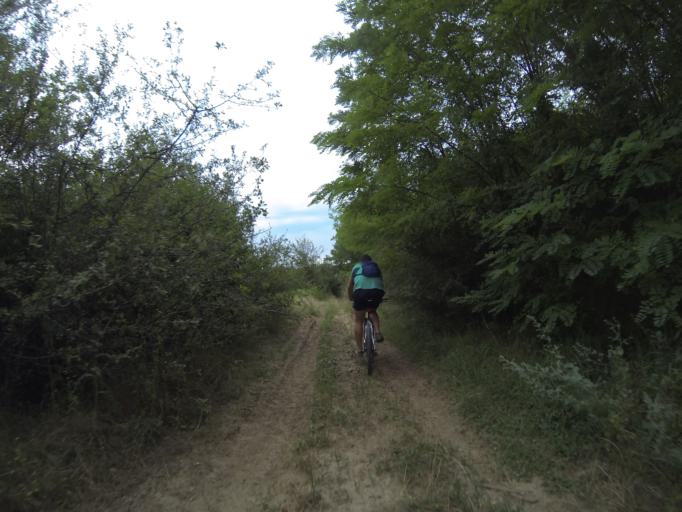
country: RO
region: Dolj
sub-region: Comuna Almaju
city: Almaju
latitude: 44.4746
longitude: 23.6932
